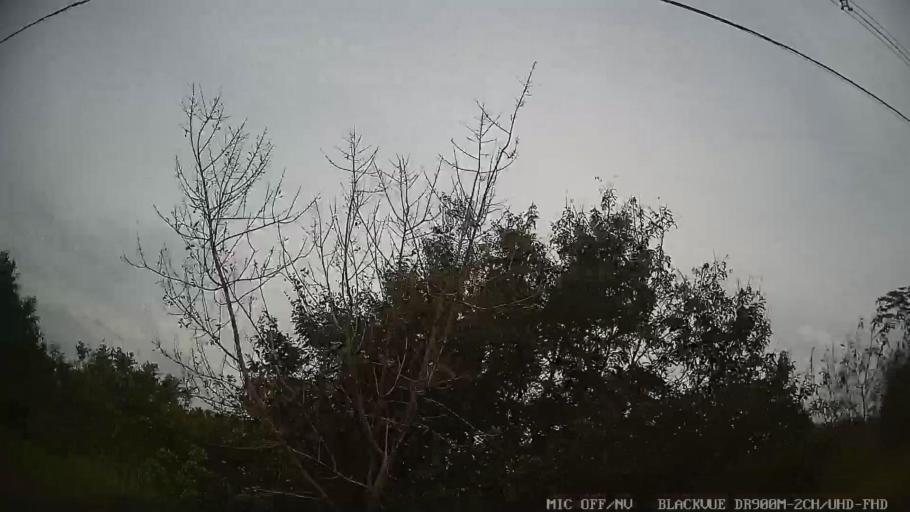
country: BR
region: Sao Paulo
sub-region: Indaiatuba
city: Indaiatuba
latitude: -23.0958
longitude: -47.2580
